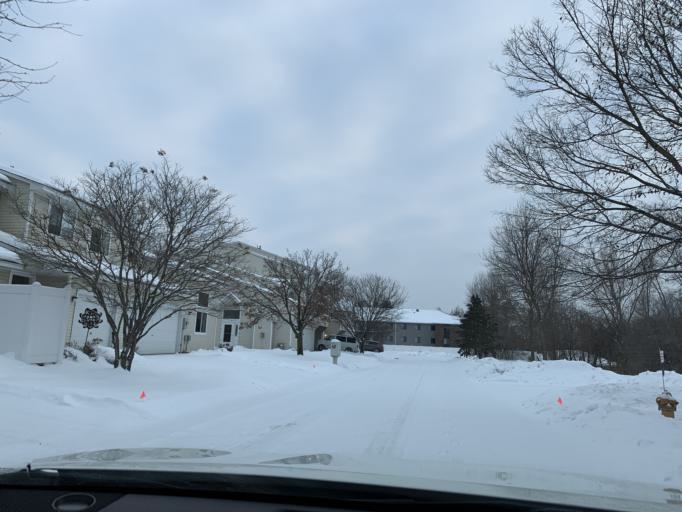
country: US
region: Minnesota
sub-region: Anoka County
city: Coon Rapids
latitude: 45.1652
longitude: -93.2927
